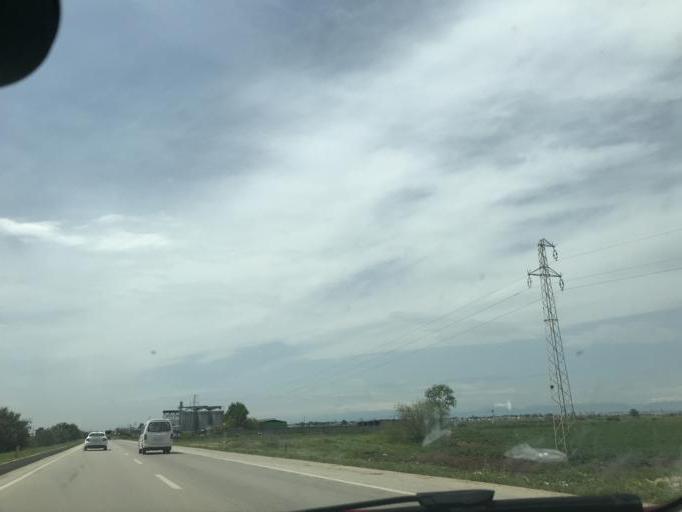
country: TR
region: Adana
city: Yuregir
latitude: 36.9771
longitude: 35.4751
